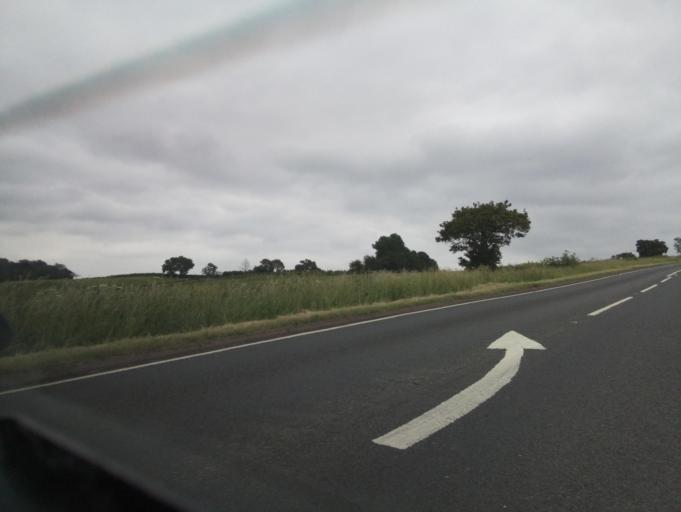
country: GB
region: England
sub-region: Leicestershire
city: Melton Mowbray
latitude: 52.7217
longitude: -0.8350
